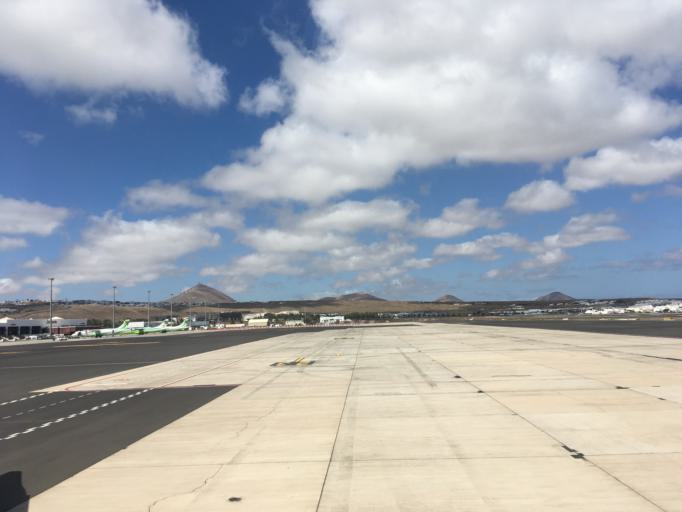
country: ES
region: Canary Islands
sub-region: Provincia de Las Palmas
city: Tias
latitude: 28.9489
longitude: -13.6064
